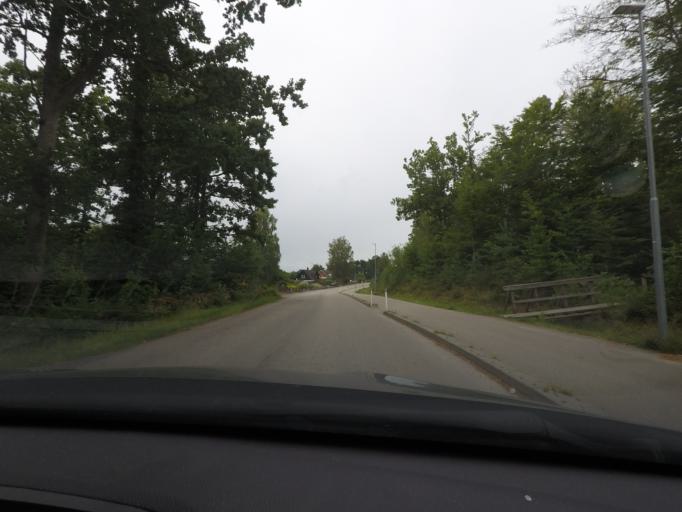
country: SE
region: Skane
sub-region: Osby Kommun
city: Osby
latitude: 56.3666
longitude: 14.0022
